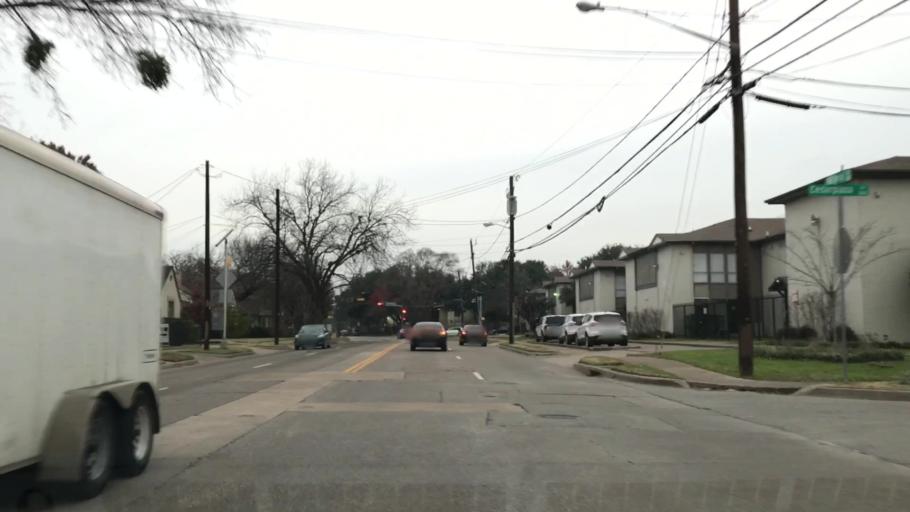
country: US
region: Texas
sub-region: Dallas County
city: Highland Park
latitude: 32.8221
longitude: -96.8263
